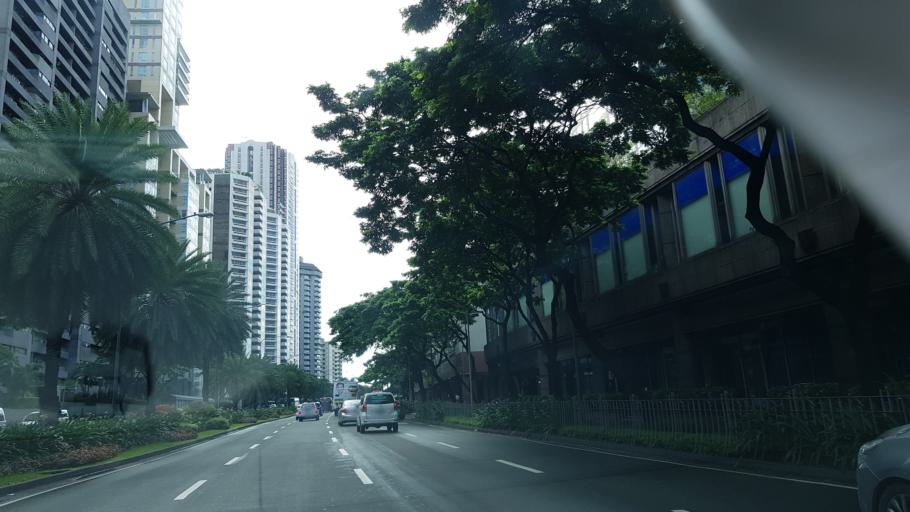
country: PH
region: Metro Manila
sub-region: Makati City
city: Makati City
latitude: 14.5541
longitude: 121.0252
